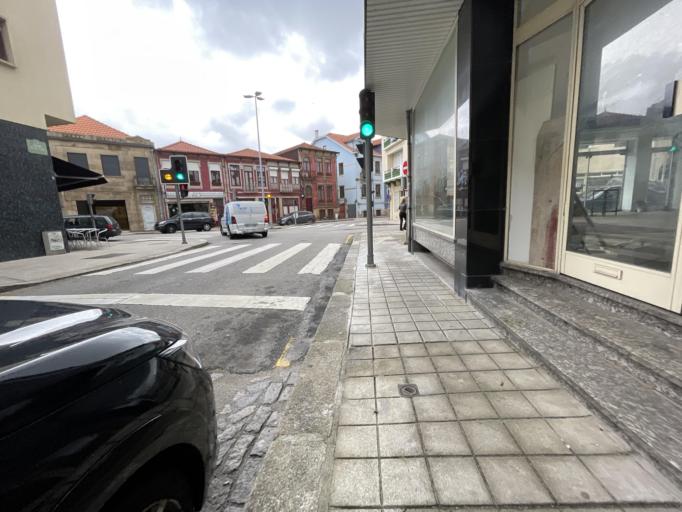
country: PT
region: Porto
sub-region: Porto
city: Porto
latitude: 41.1674
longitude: -8.6109
